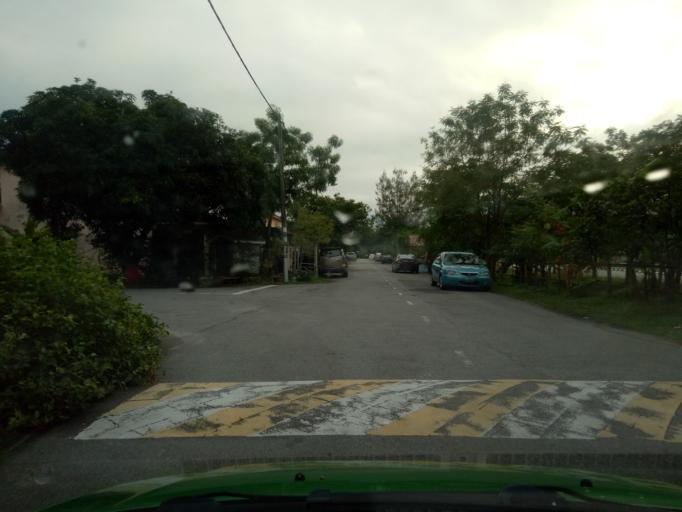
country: MY
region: Selangor
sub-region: Hulu Langat
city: Semenyih
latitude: 2.9286
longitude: 101.8638
